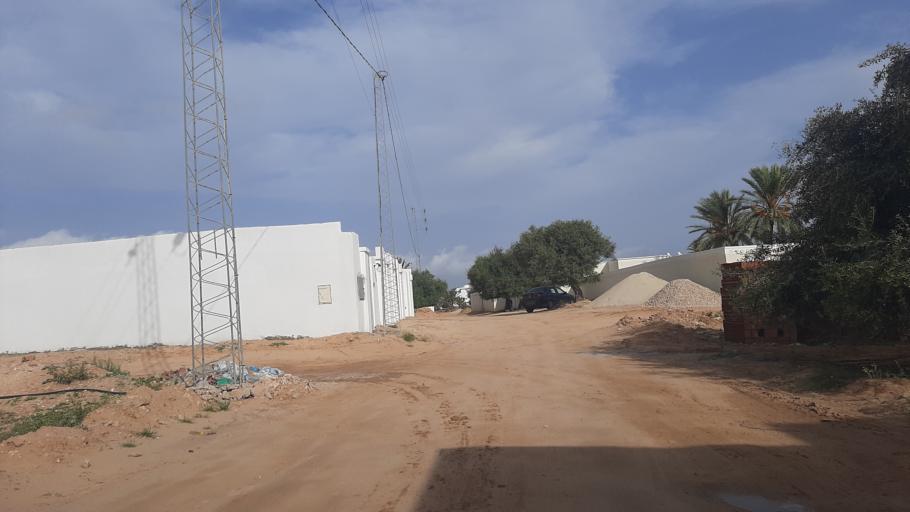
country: TN
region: Madanin
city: Midoun
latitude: 33.8014
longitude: 11.0265
